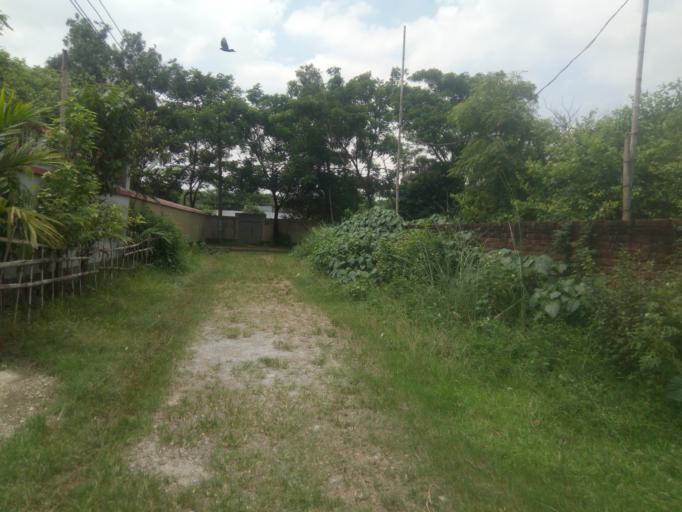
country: BD
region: Dhaka
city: Azimpur
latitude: 23.7517
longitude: 90.3472
